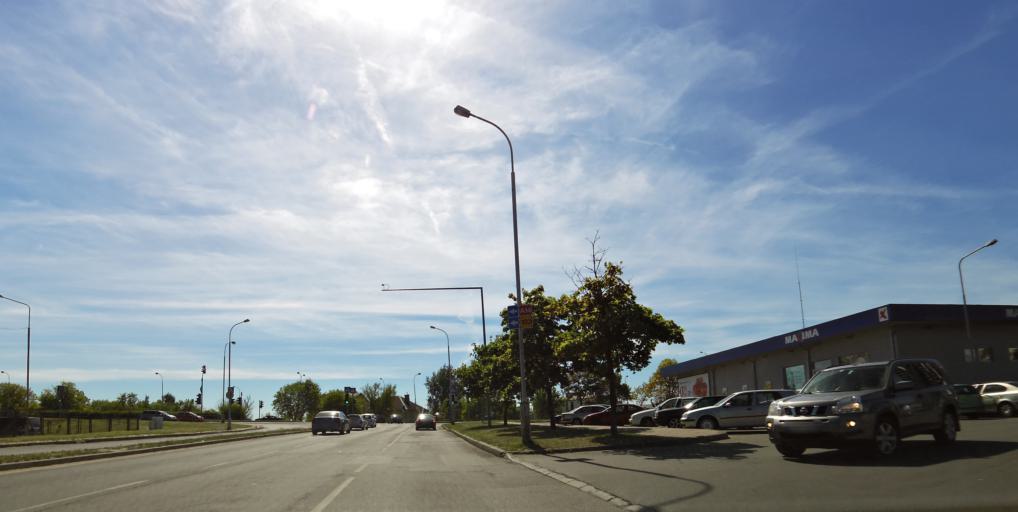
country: LT
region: Vilnius County
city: Seskine
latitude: 54.7109
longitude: 25.2489
